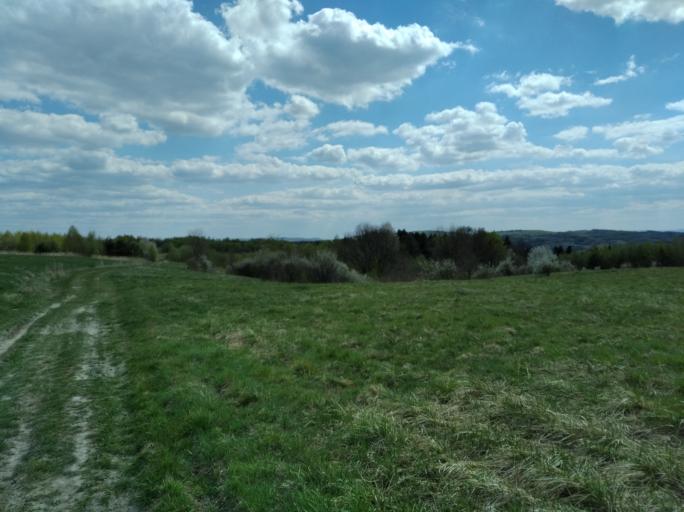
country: PL
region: Subcarpathian Voivodeship
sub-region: Powiat brzozowski
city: Golcowa
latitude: 49.7535
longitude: 22.0743
